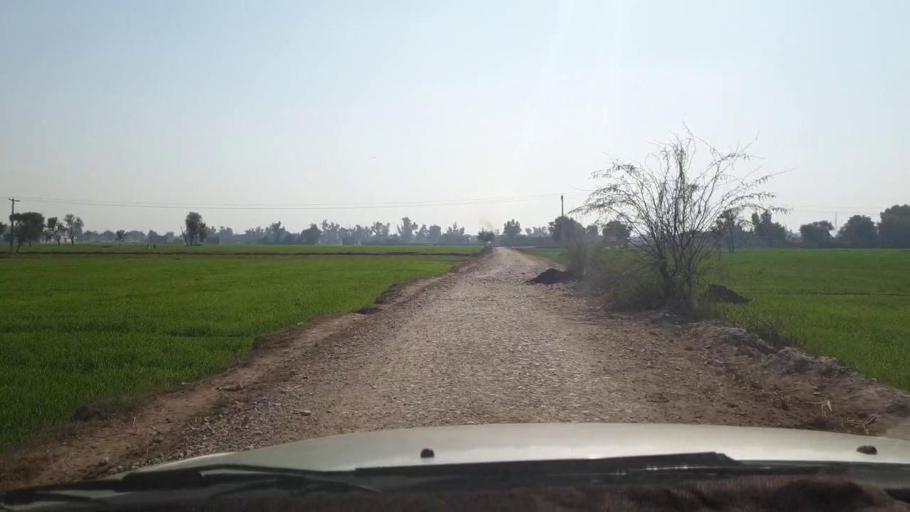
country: PK
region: Sindh
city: Mirpur Mathelo
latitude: 28.0358
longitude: 69.5515
